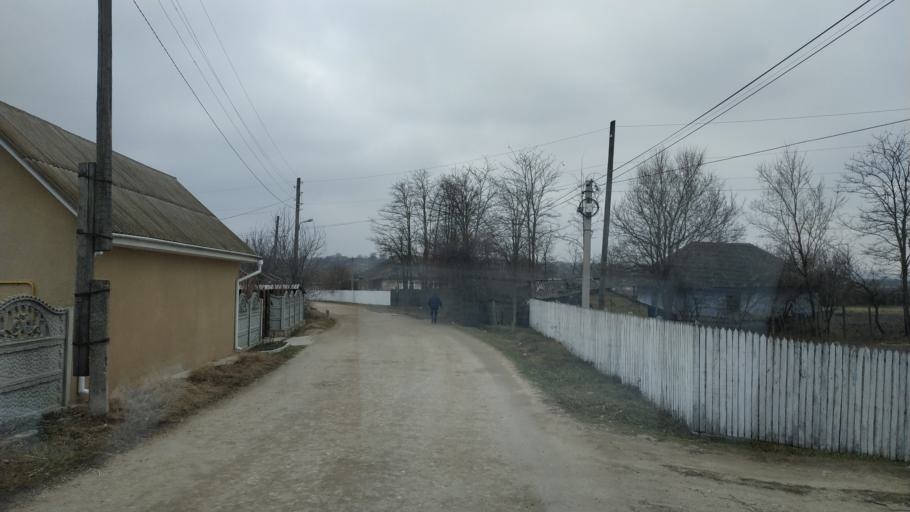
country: MD
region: Hincesti
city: Hincesti
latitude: 46.8841
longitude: 28.4065
